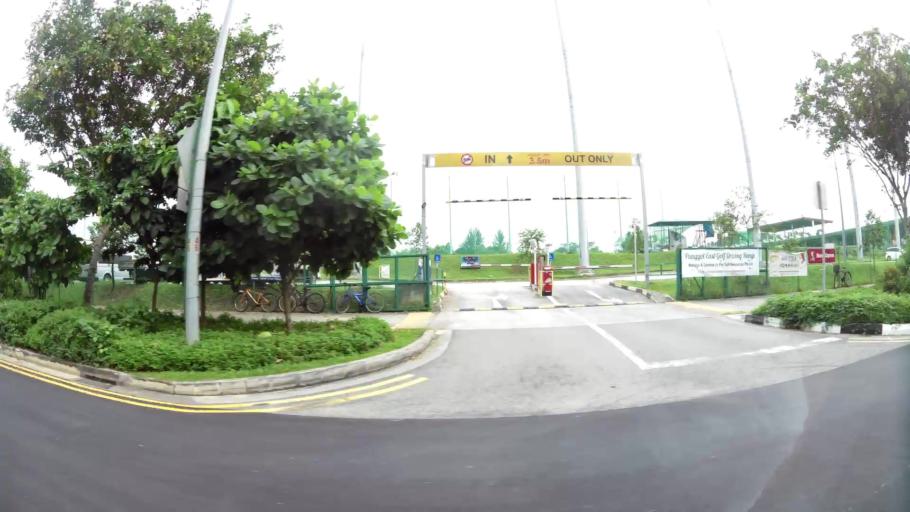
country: MY
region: Johor
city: Kampung Pasir Gudang Baru
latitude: 1.3962
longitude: 103.9175
